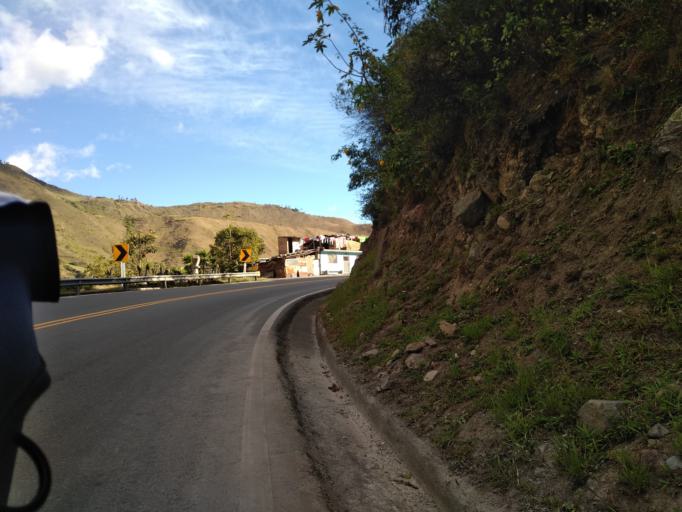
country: CO
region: Narino
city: Funes
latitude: 1.0517
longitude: -77.4506
